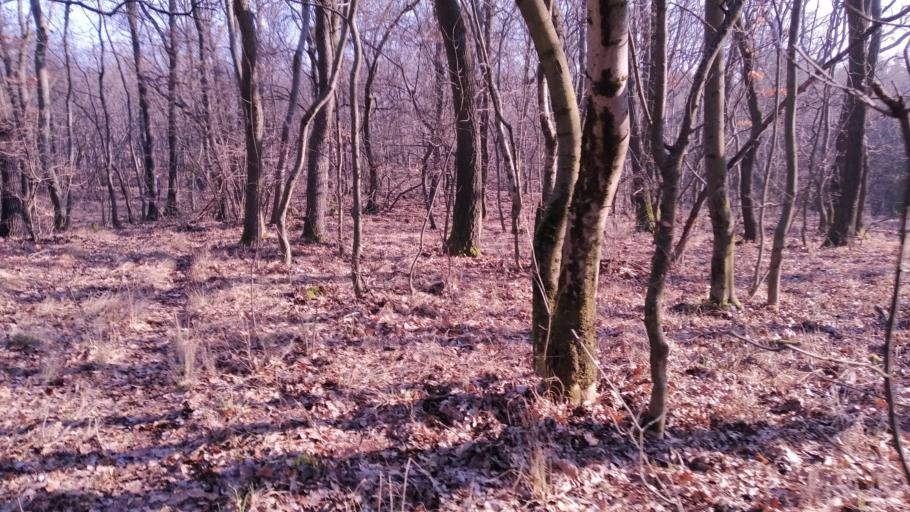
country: HU
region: Pest
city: Solymar
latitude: 47.5777
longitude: 18.9459
